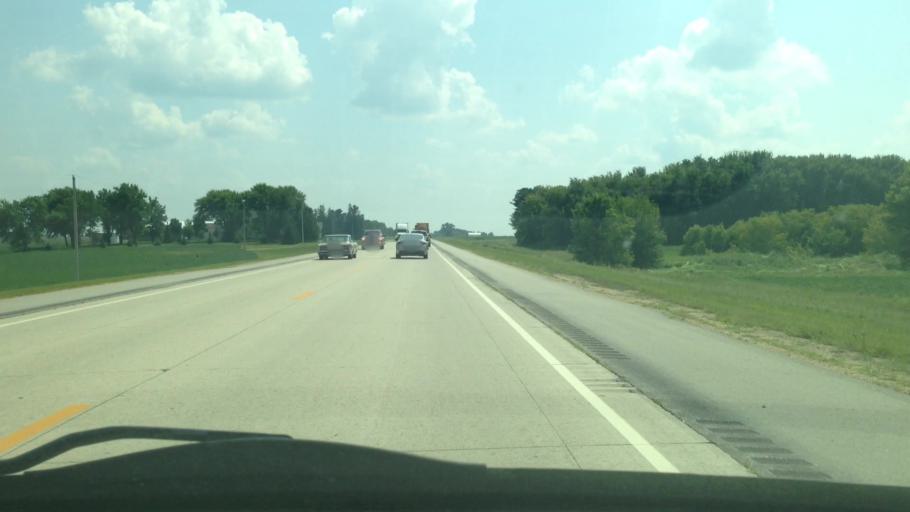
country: US
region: Minnesota
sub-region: Fillmore County
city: Spring Valley
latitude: 43.5257
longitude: -92.3694
